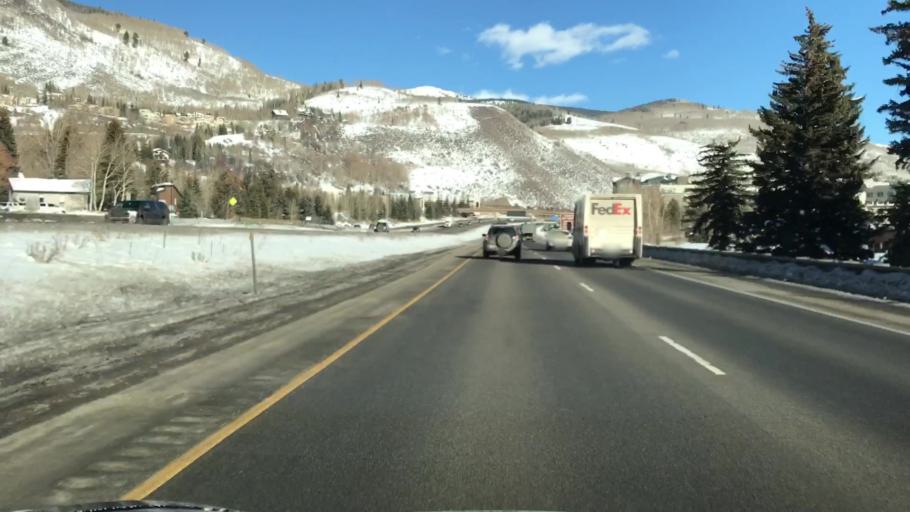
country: US
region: Colorado
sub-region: Eagle County
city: Vail
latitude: 39.6422
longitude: -106.3967
